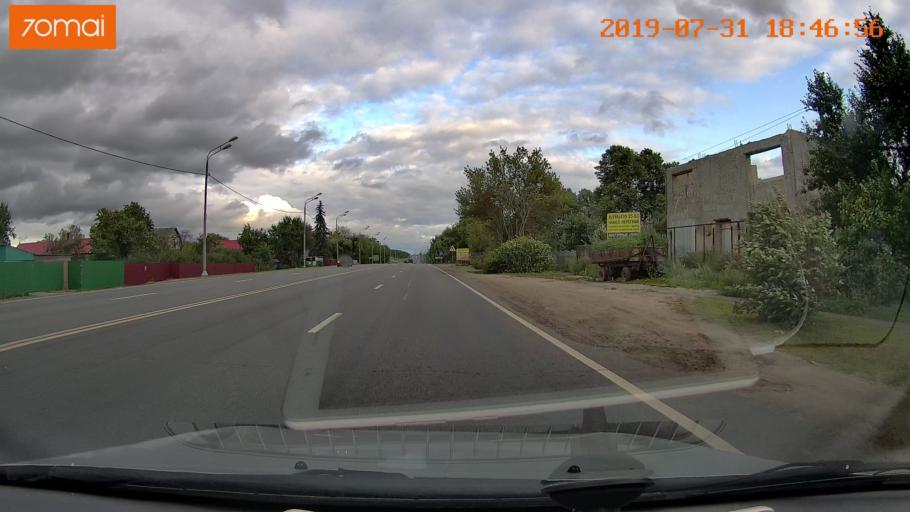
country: RU
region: Moskovskaya
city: Troitskoye
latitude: 55.2429
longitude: 38.5356
